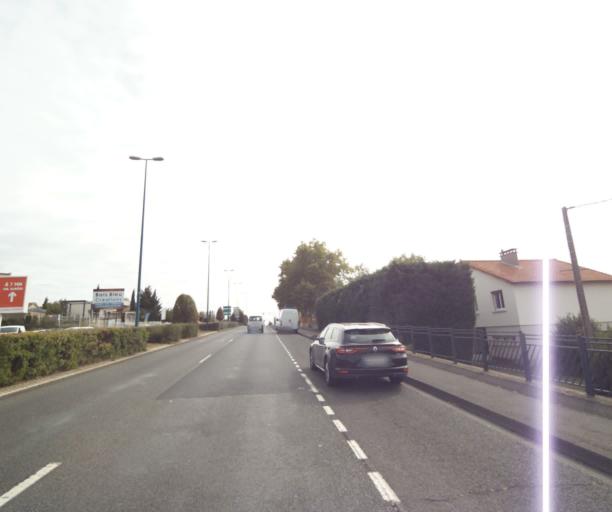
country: FR
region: Auvergne
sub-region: Departement du Puy-de-Dome
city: Aubiere
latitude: 45.7750
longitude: 3.1192
